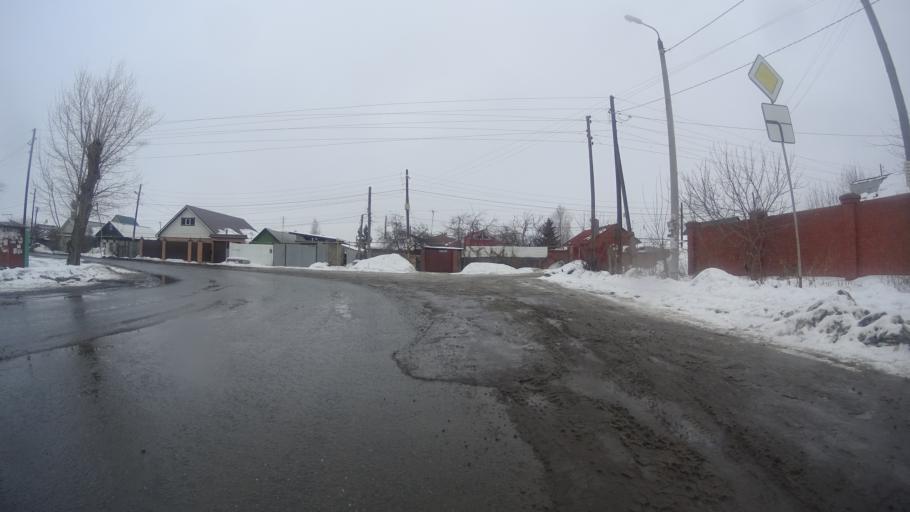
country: RU
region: Chelyabinsk
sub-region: Gorod Chelyabinsk
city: Chelyabinsk
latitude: 55.1286
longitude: 61.3927
